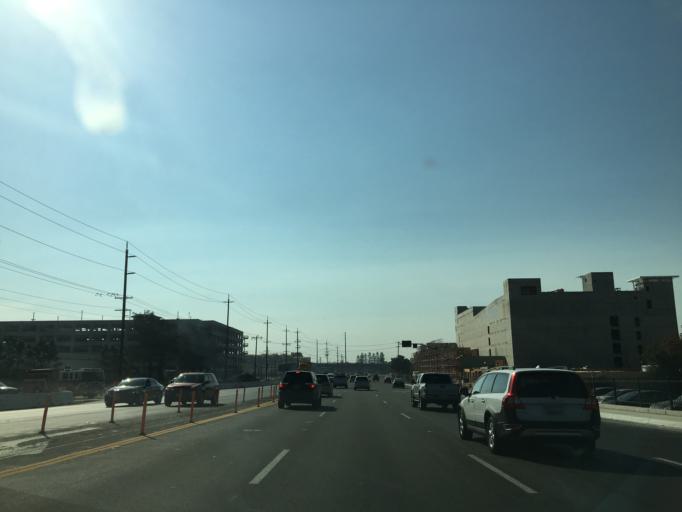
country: US
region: California
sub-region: Santa Clara County
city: Milpitas
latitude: 37.4122
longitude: -121.8879
